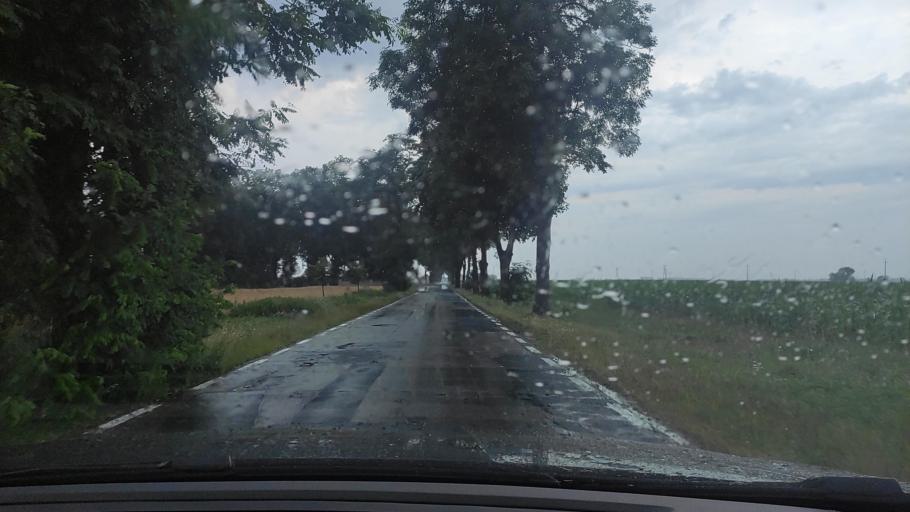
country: PL
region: Greater Poland Voivodeship
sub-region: Powiat poznanski
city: Kleszczewo
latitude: 52.2898
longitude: 17.1864
